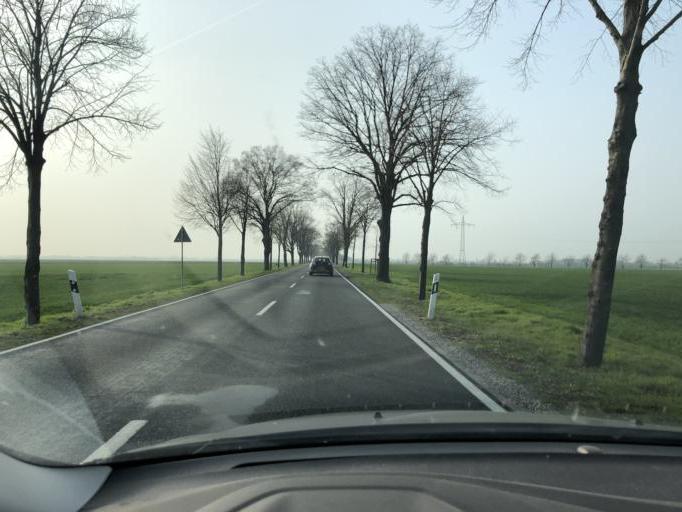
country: DE
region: Saxony-Anhalt
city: Roitzsch
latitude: 51.5418
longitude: 12.2652
